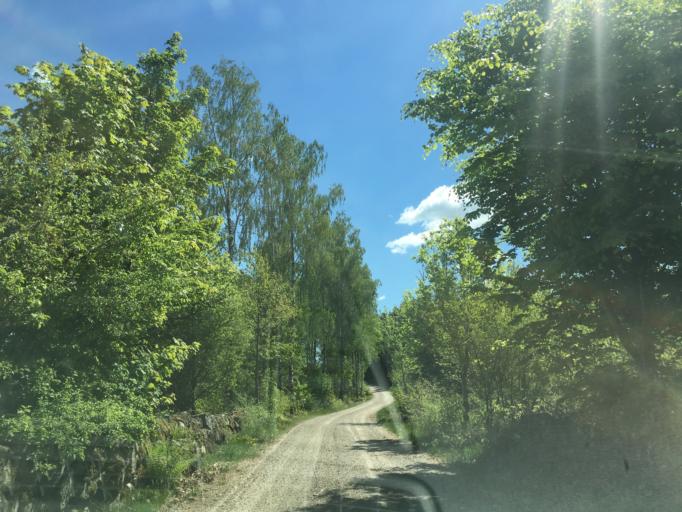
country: SE
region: Blekinge
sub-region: Olofstroms Kommun
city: Olofstroem
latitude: 56.4043
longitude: 14.5772
